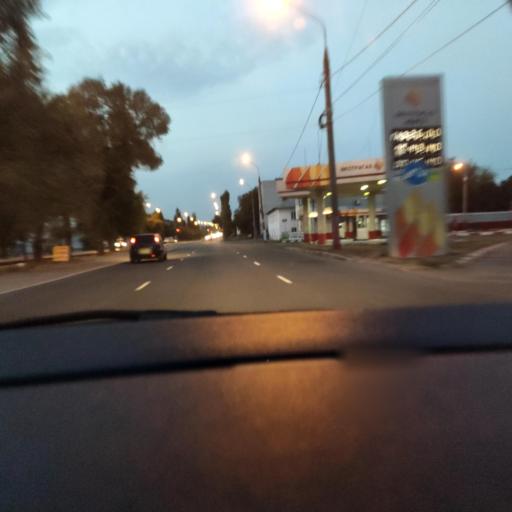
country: RU
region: Voronezj
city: Voronezh
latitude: 51.6796
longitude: 39.1666
